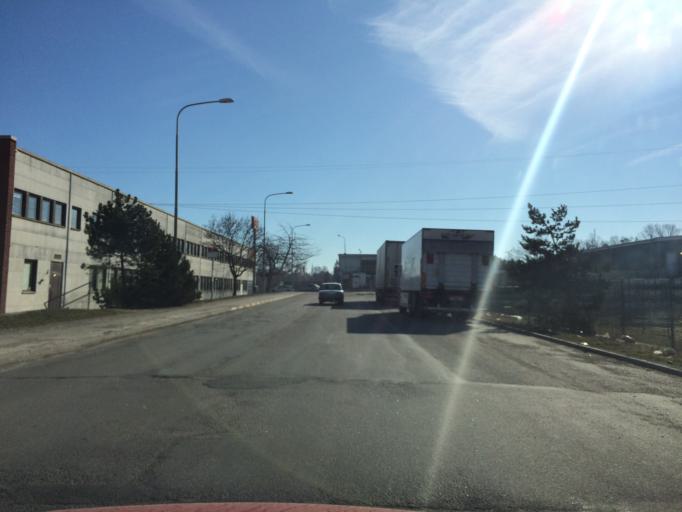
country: SE
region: Stockholm
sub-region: Huddinge Kommun
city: Segeltorp
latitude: 59.2868
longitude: 17.9378
